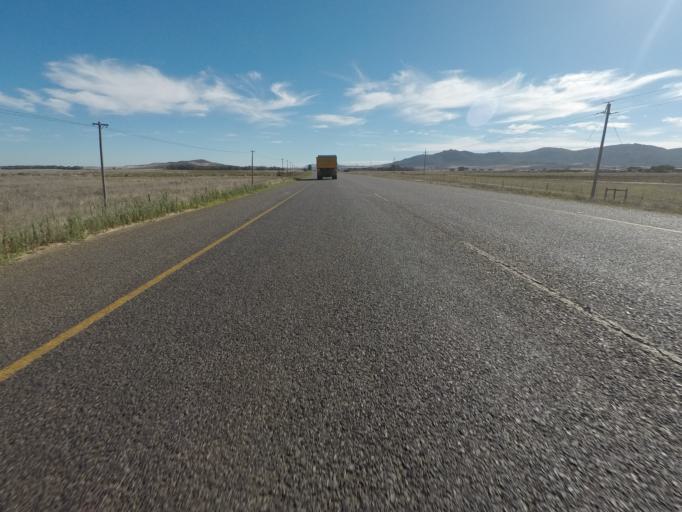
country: ZA
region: Western Cape
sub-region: West Coast District Municipality
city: Malmesbury
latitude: -33.6309
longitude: 18.7222
